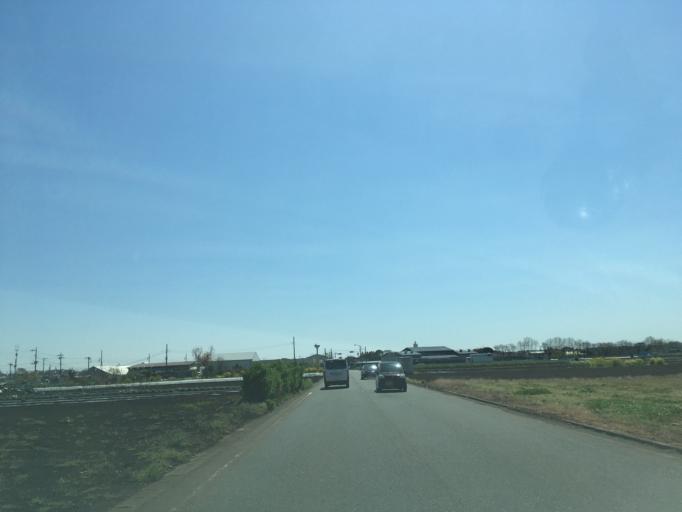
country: JP
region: Tokyo
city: Hachioji
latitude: 35.5705
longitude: 139.3265
